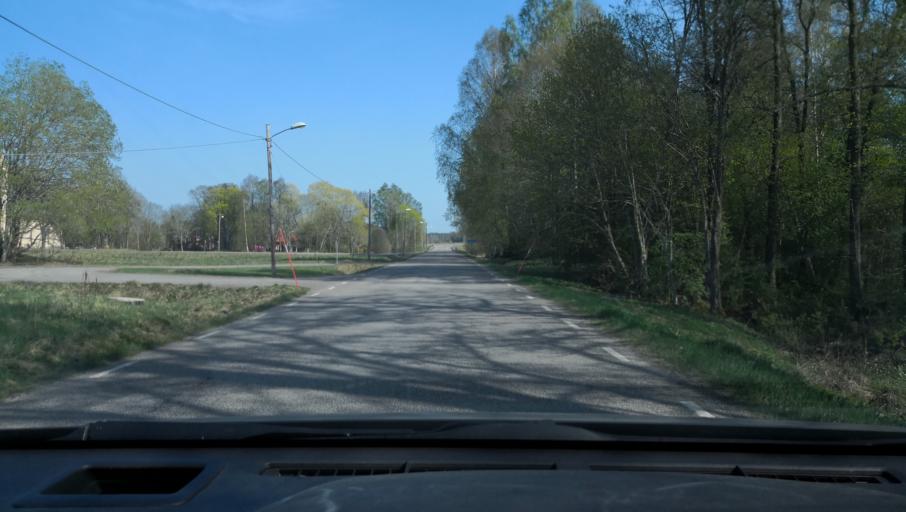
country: SE
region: Uppsala
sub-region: Heby Kommun
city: Heby
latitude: 60.0345
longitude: 16.7960
